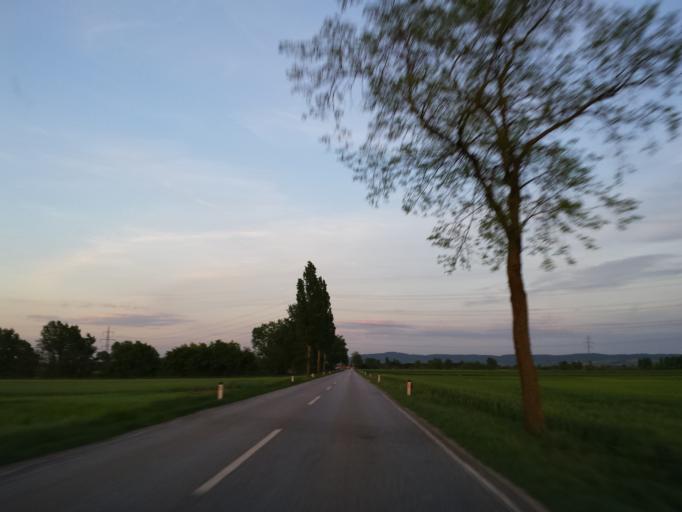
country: AT
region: Lower Austria
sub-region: Politischer Bezirk Tulln
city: Langenrohr
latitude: 48.3234
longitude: 15.9825
